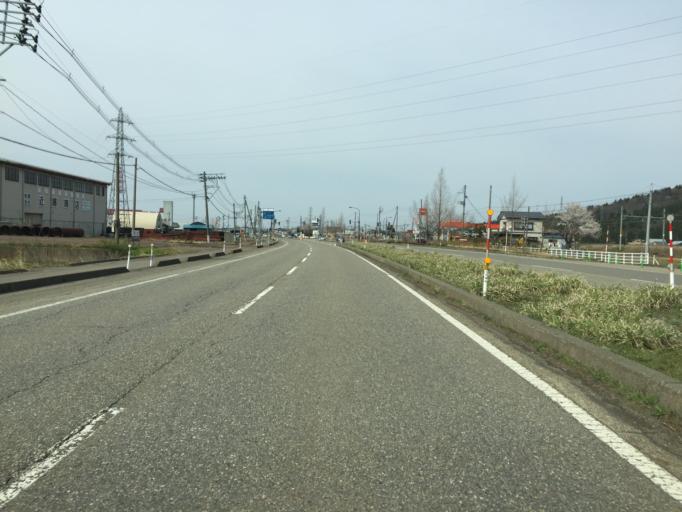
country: JP
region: Niigata
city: Ojiya
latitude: 37.3619
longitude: 138.8338
